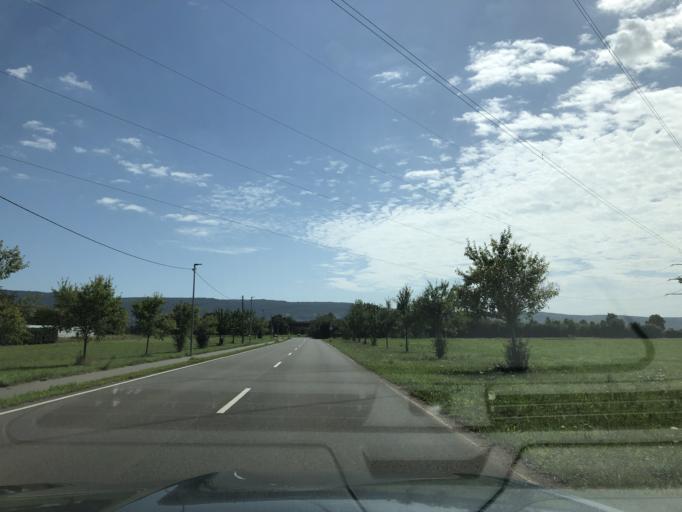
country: DE
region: Baden-Wuerttemberg
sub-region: Karlsruhe Region
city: Eppelheim
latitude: 49.3767
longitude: 8.6421
